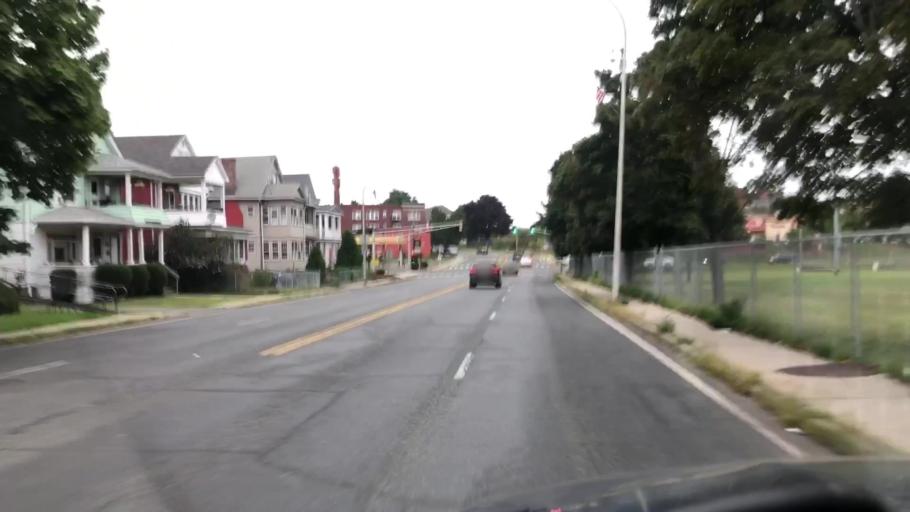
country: US
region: Massachusetts
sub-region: Hampden County
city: Holyoke
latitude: 42.2018
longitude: -72.6219
